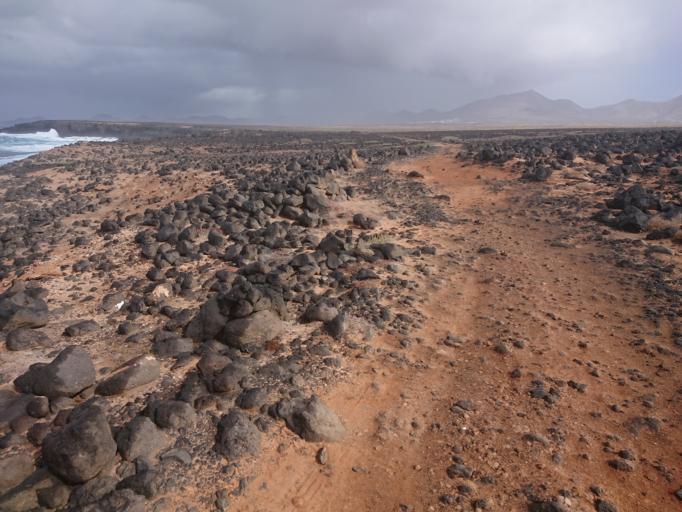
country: ES
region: Canary Islands
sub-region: Provincia de Las Palmas
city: Playa Blanca
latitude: 28.8953
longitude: -13.8598
